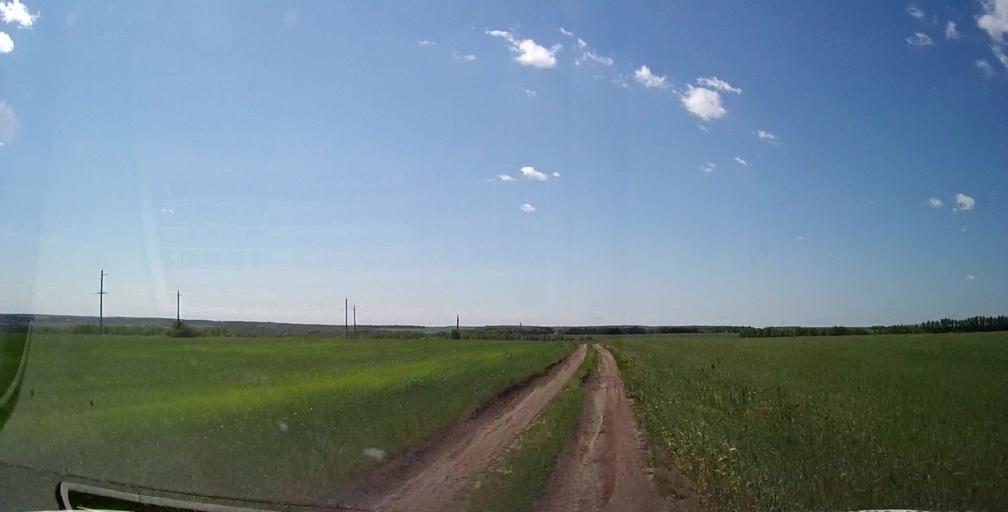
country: RU
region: Tula
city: Kurkino
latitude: 53.1580
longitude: 38.4810
